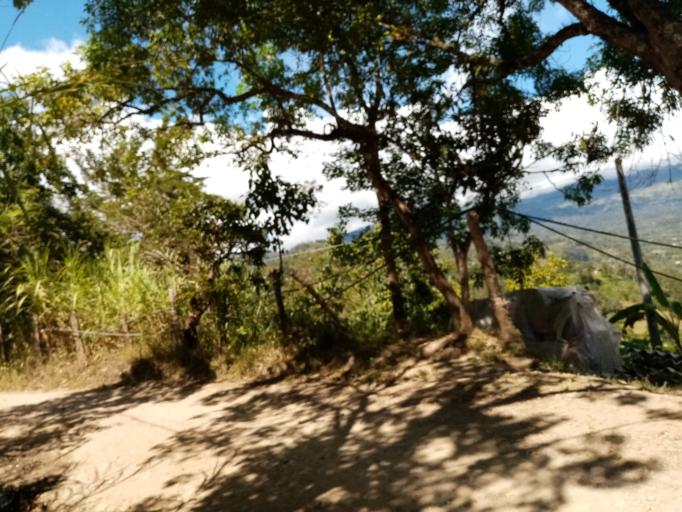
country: CO
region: Cundinamarca
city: Tenza
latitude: 5.0779
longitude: -73.4297
